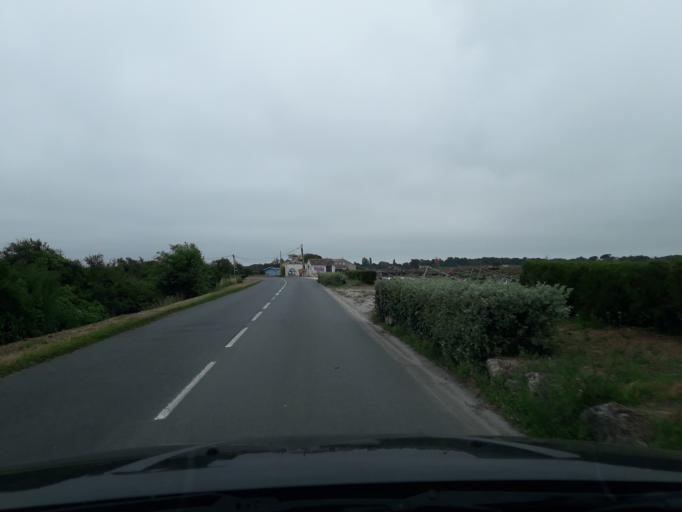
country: FR
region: Poitou-Charentes
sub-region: Departement de la Charente-Maritime
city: Boyard-Ville
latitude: 45.9617
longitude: -1.2480
